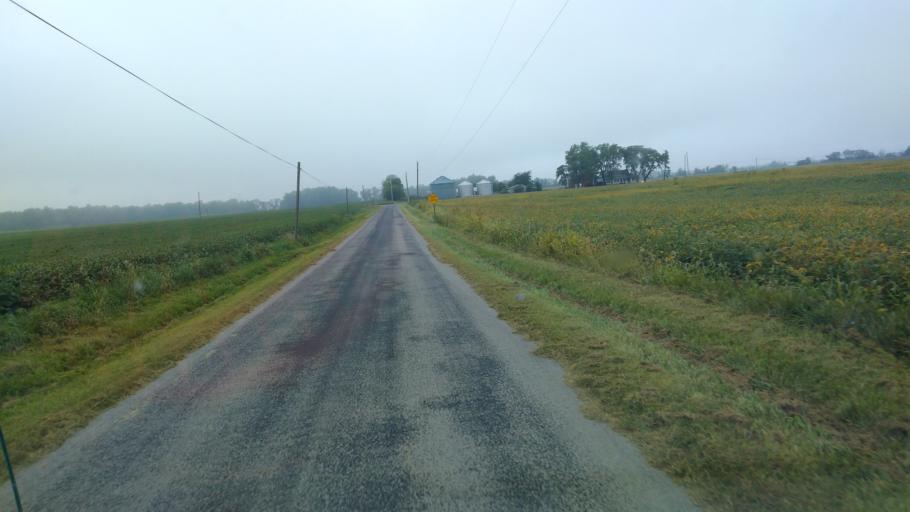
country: US
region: Ohio
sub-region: Hardin County
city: Kenton
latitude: 40.5232
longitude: -83.6011
